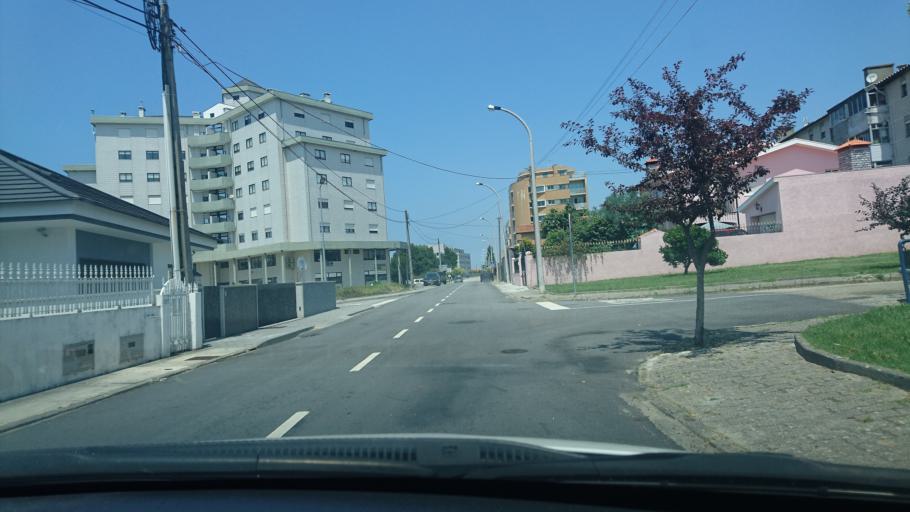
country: PT
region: Aveiro
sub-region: Ovar
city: Esmoriz
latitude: 40.9544
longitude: -8.6301
